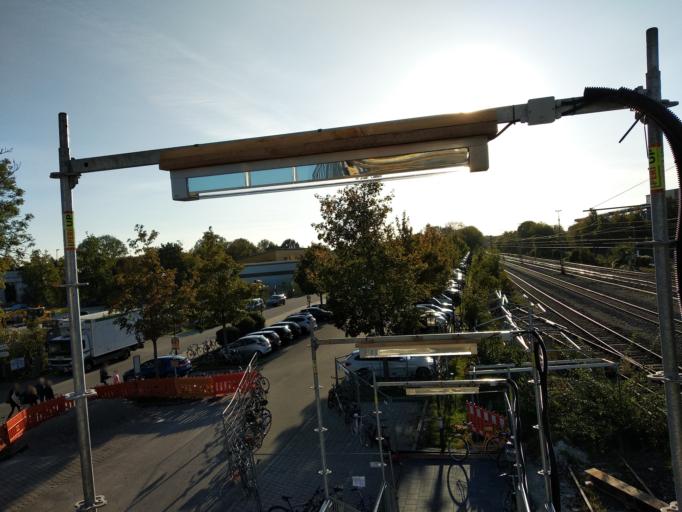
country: DE
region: Bavaria
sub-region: Upper Bavaria
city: Feldkirchen
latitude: 48.1513
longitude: 11.7304
